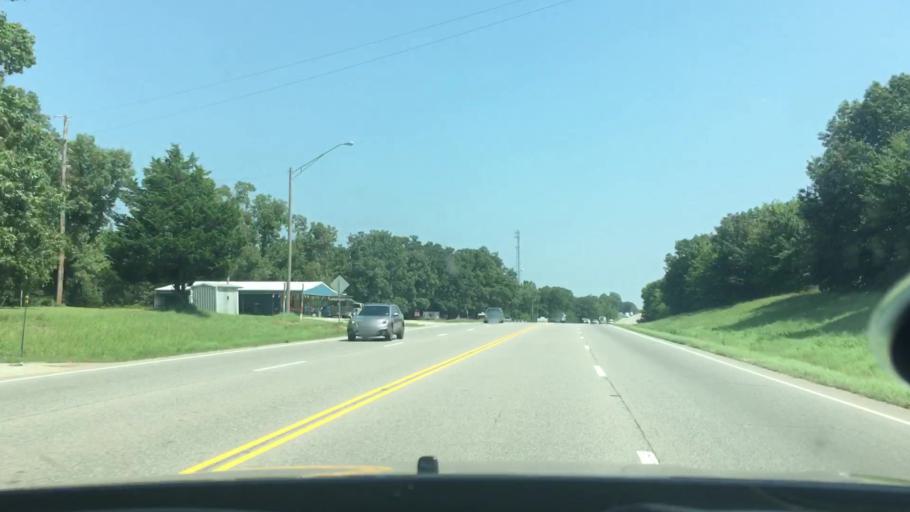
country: US
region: Oklahoma
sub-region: Atoka County
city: Atoka
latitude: 34.3247
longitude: -96.1648
